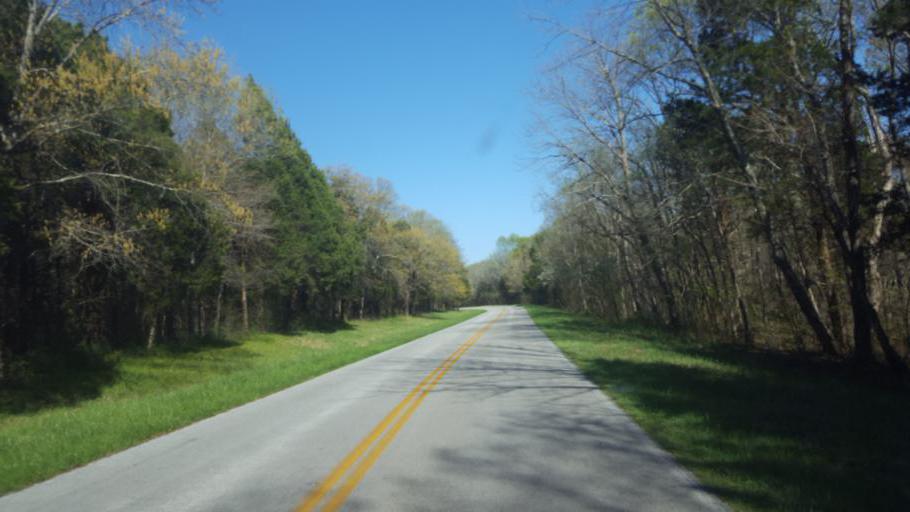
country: US
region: Kentucky
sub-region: Barren County
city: Cave City
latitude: 37.1524
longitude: -86.1095
